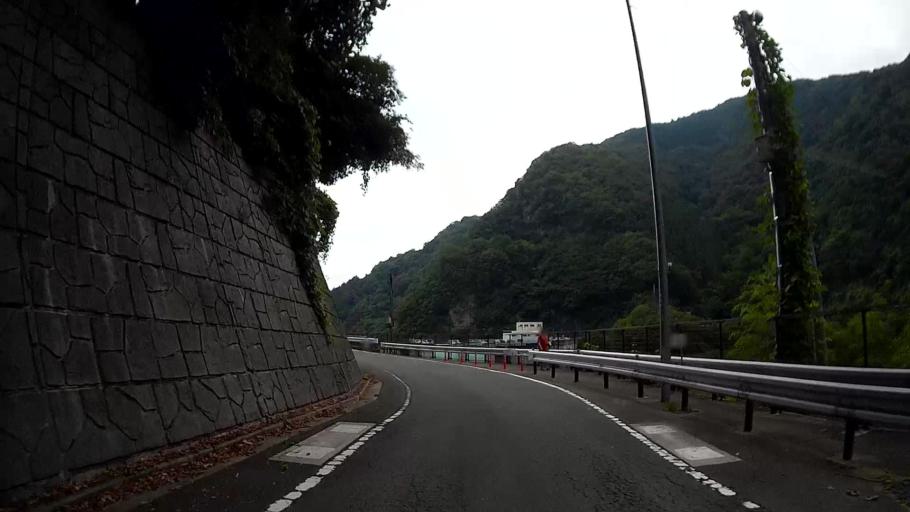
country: JP
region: Saitama
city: Chichibu
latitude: 35.9412
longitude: 138.9078
